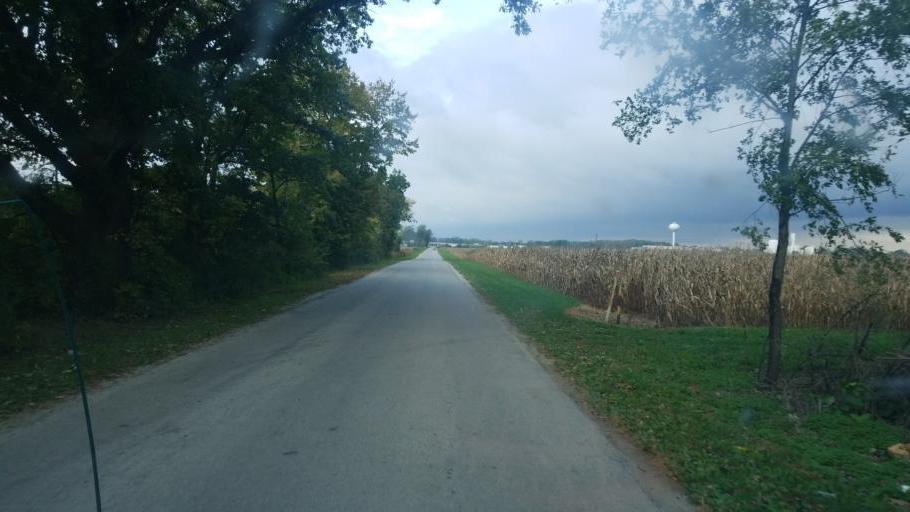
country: US
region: Ohio
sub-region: Wood County
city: North Baltimore
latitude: 41.1822
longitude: -83.6340
